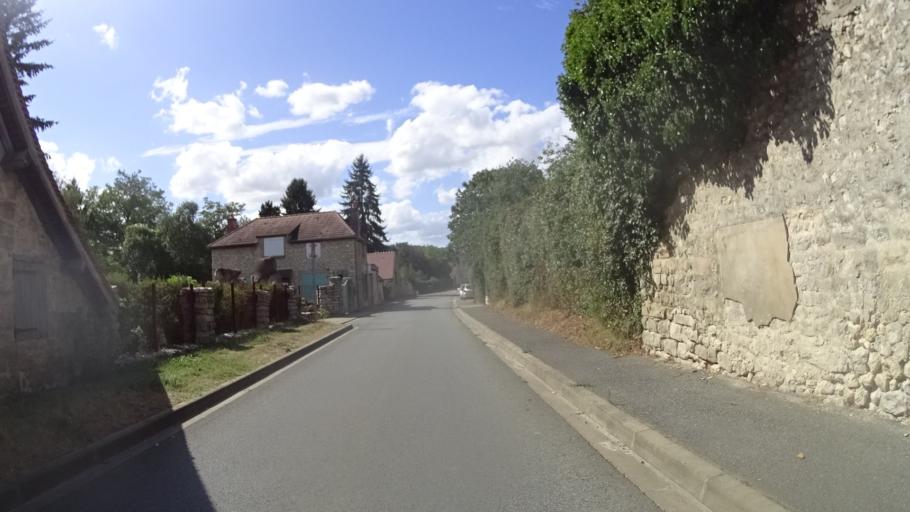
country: FR
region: Ile-de-France
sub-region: Departement de l'Essonne
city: Boutigny-sur-Essonne
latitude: 48.4538
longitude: 2.3634
